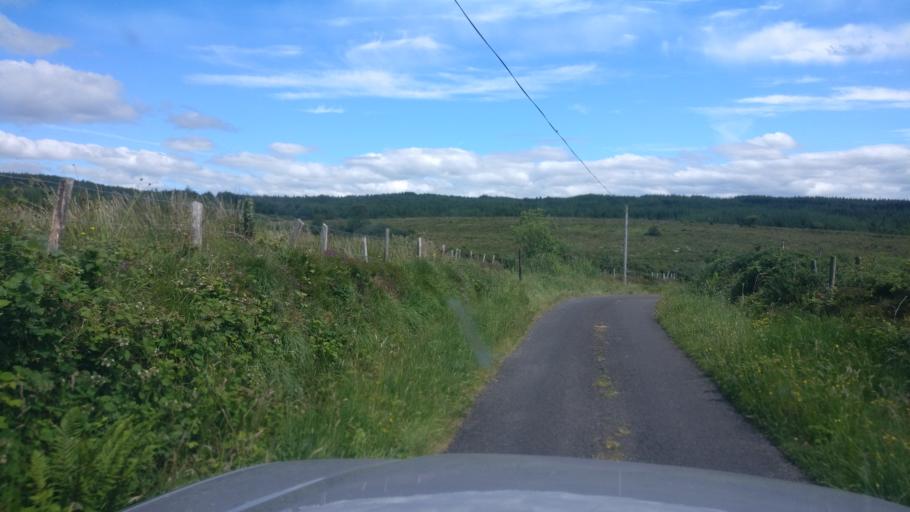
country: IE
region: Connaught
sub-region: County Galway
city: Gort
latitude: 53.0717
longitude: -8.7048
